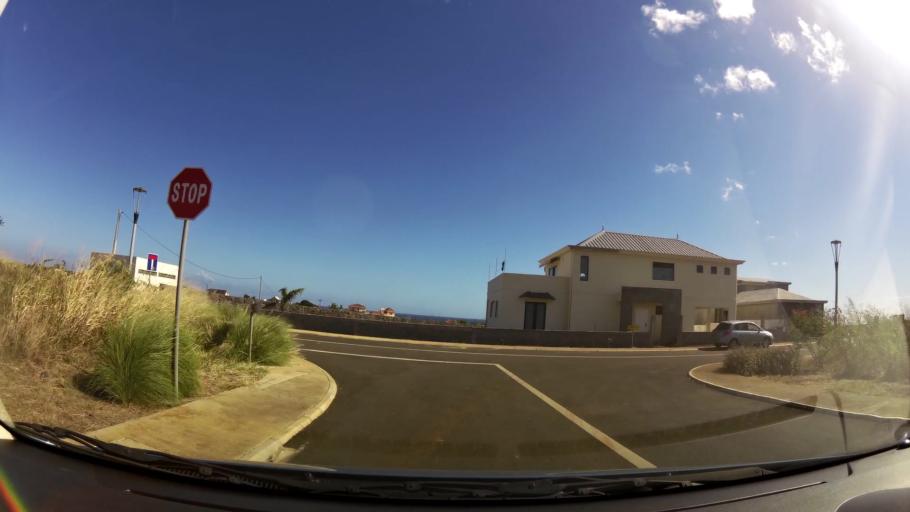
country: MU
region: Black River
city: Flic en Flac
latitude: -20.2693
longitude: 57.3786
